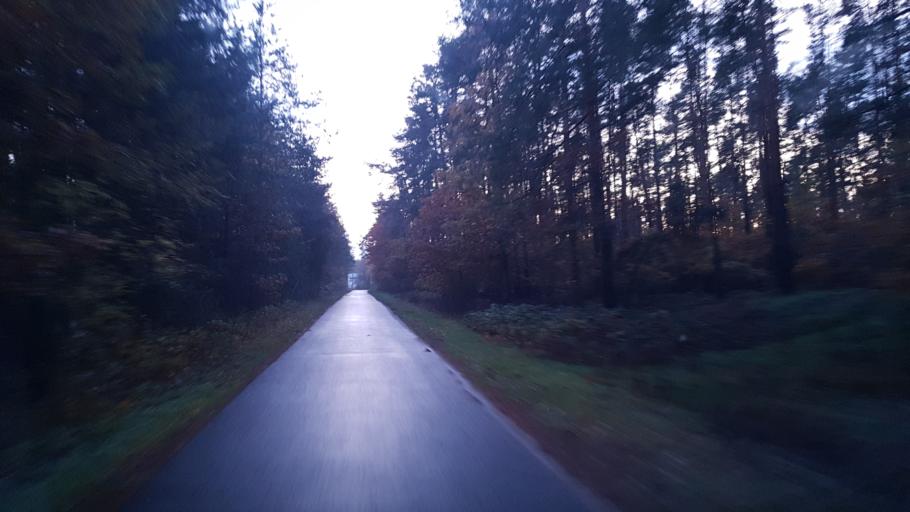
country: DE
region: Brandenburg
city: Herzberg
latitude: 51.6362
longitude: 13.2103
